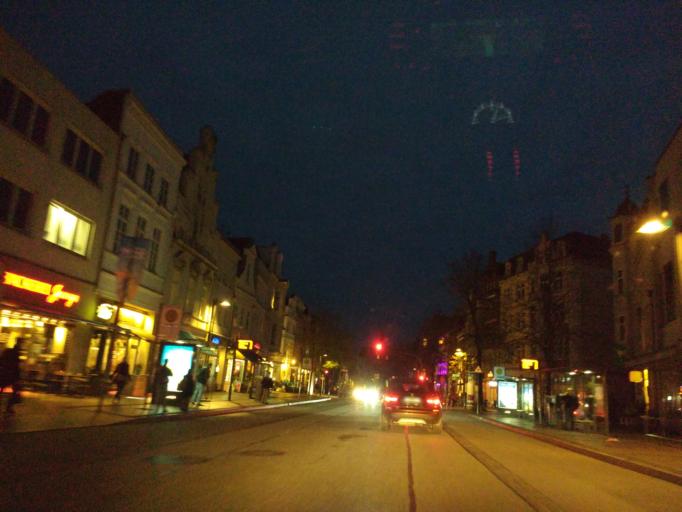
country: DE
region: Schleswig-Holstein
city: Luebeck
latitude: 53.8631
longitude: 10.6868
